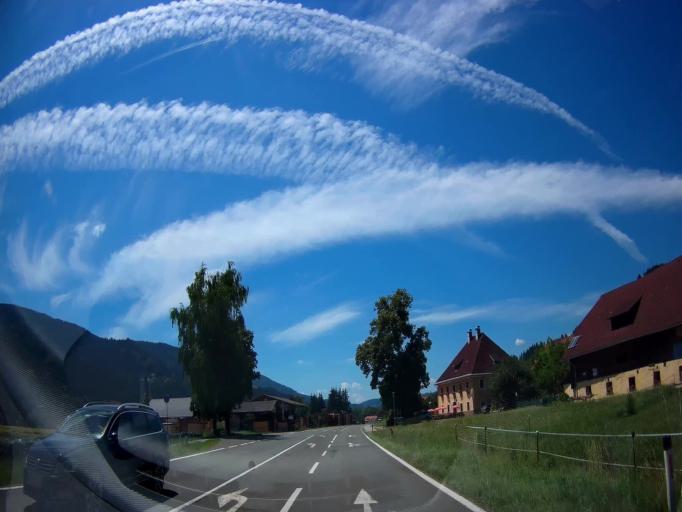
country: AT
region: Carinthia
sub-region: Politischer Bezirk Sankt Veit an der Glan
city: Micheldorf
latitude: 46.9025
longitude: 14.3875
